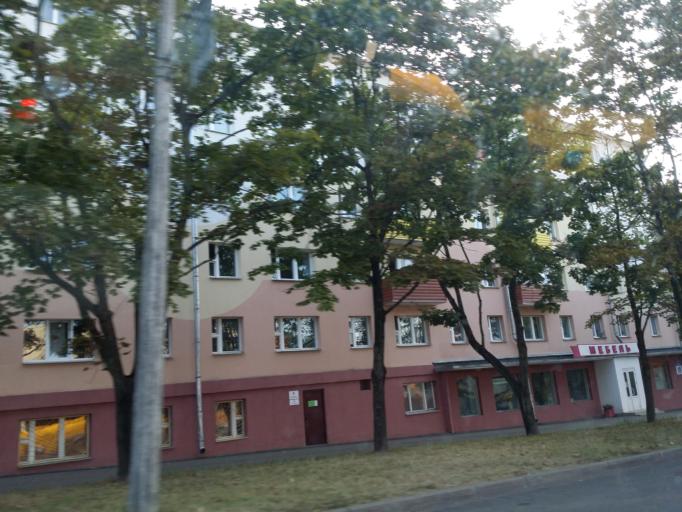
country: BY
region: Minsk
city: Minsk
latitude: 53.9133
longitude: 27.5921
